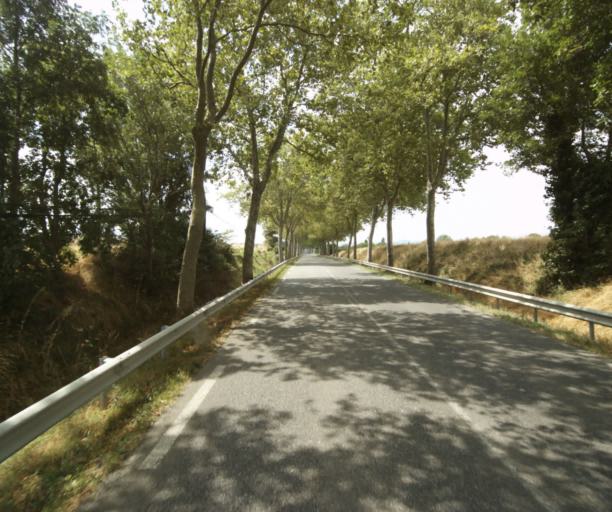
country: FR
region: Midi-Pyrenees
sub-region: Departement de la Haute-Garonne
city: Revel
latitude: 43.4502
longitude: 1.9738
